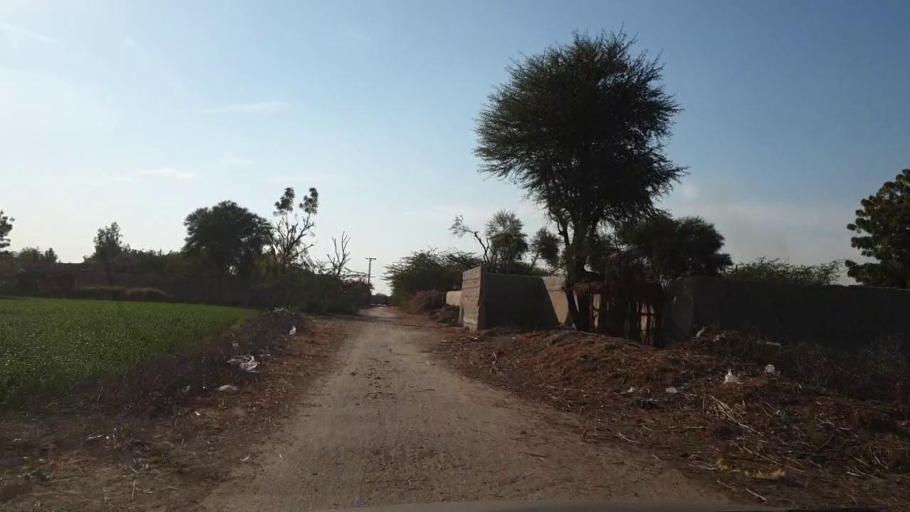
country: PK
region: Sindh
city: Khadro
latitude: 26.2157
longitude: 68.7534
